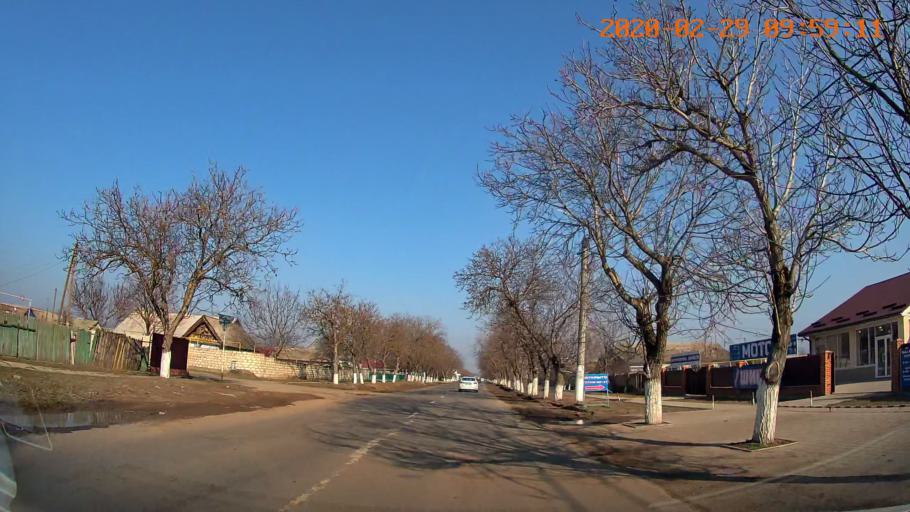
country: MD
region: Telenesti
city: Slobozia
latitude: 46.7546
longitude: 29.6889
